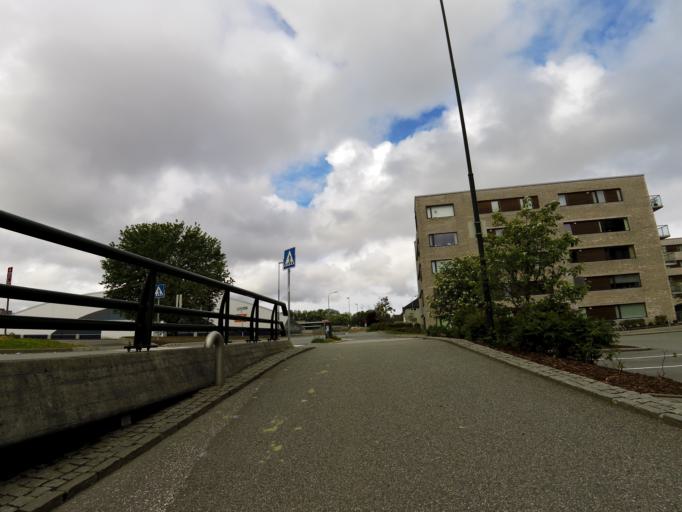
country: NO
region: Rogaland
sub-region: Stavanger
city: Stavanger
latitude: 58.9573
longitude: 5.6989
